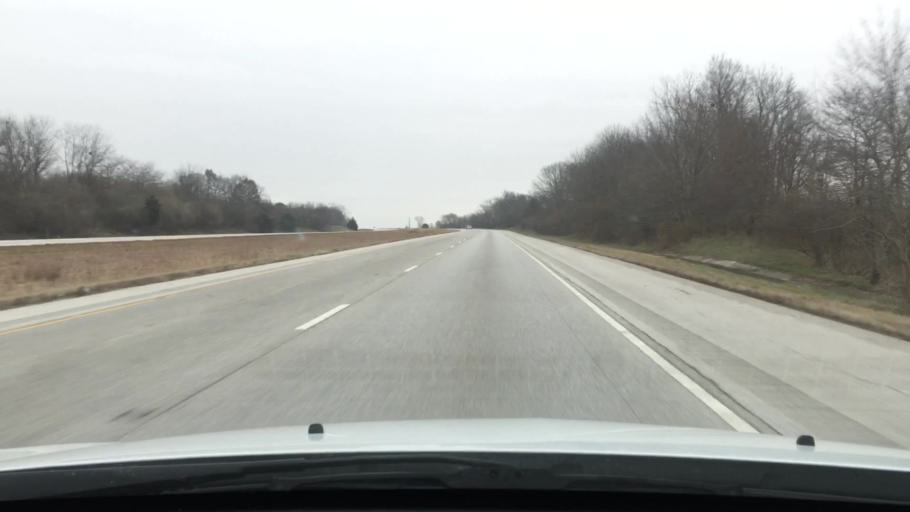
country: US
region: Illinois
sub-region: Scott County
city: Winchester
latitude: 39.6806
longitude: -90.3900
